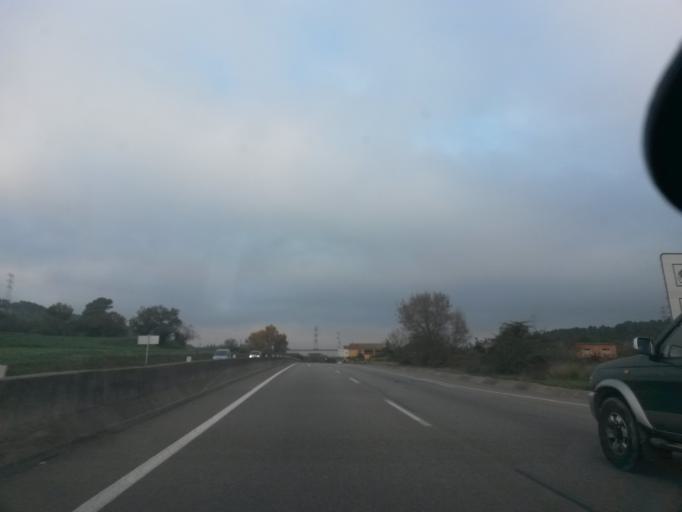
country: ES
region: Catalonia
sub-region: Provincia de Girona
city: Palol de Revardit
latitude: 42.0451
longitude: 2.8202
